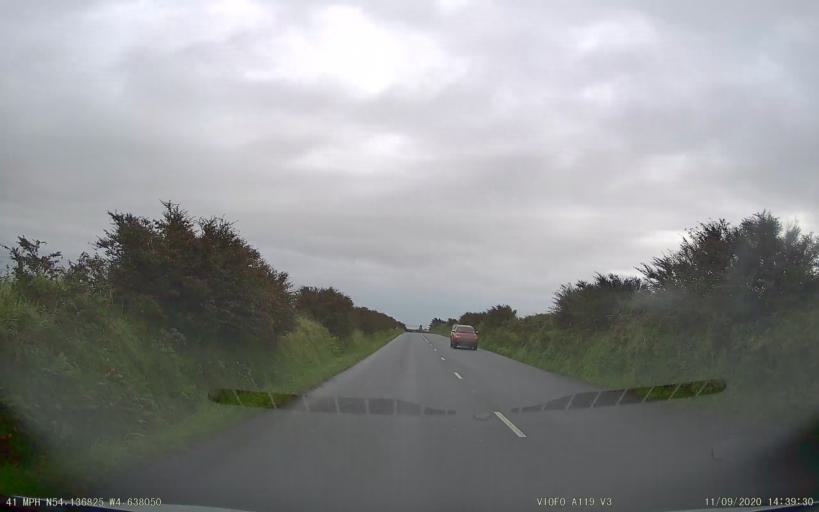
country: IM
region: Castletown
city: Castletown
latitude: 54.1369
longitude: -4.6381
